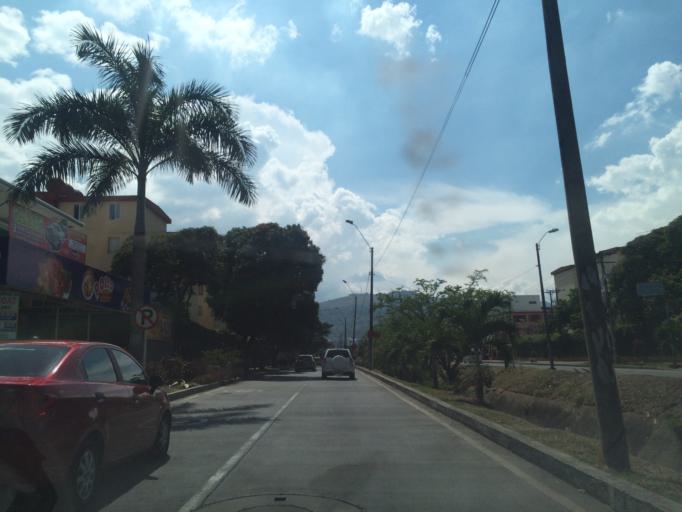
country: CO
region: Valle del Cauca
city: Cali
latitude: 3.4187
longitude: -76.5291
